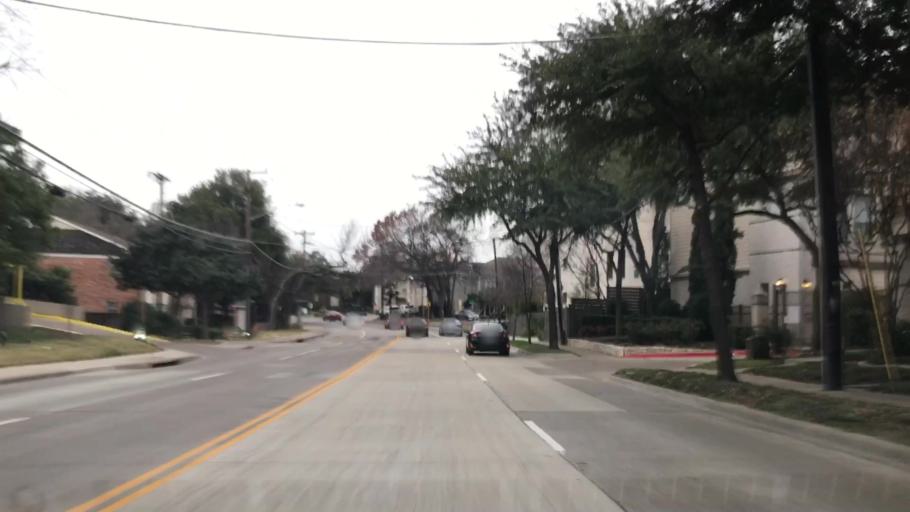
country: US
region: Texas
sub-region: Dallas County
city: Highland Park
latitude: 32.8200
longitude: -96.8217
